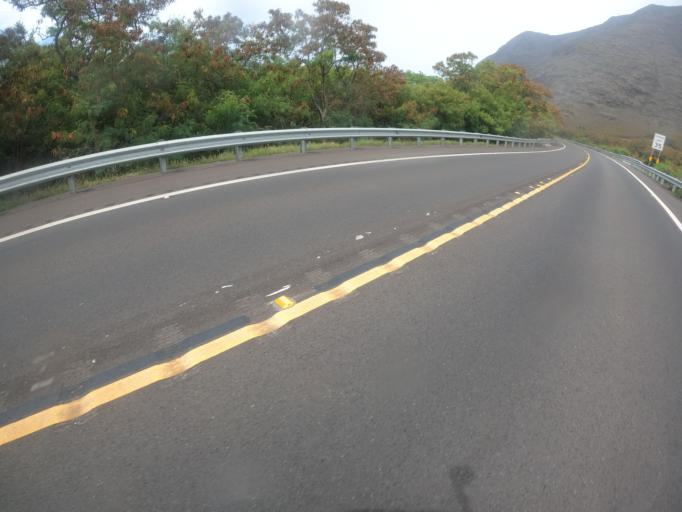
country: US
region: Hawaii
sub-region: Honolulu County
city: Makaha Valley
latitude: 21.5342
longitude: -158.2285
